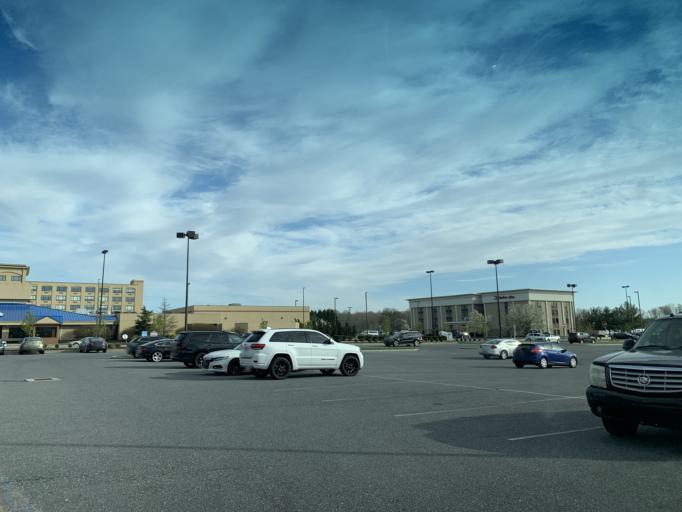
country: US
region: Delaware
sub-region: Kent County
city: Cheswold
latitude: 39.1958
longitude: -75.5514
